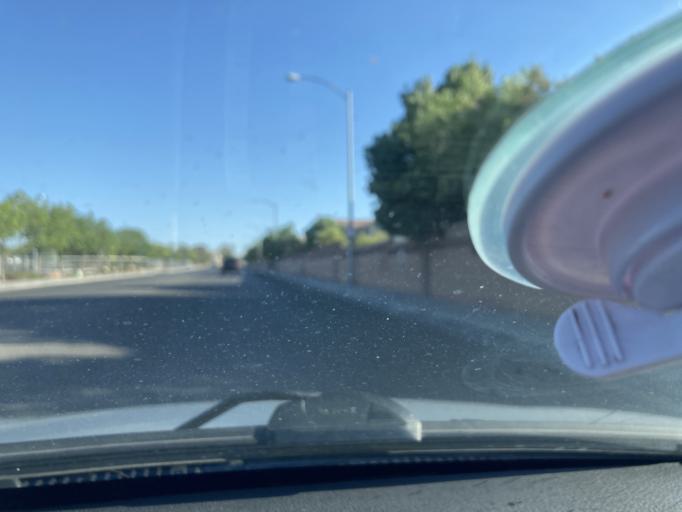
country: US
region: Nevada
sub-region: Clark County
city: Enterprise
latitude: 36.0621
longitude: -115.2930
